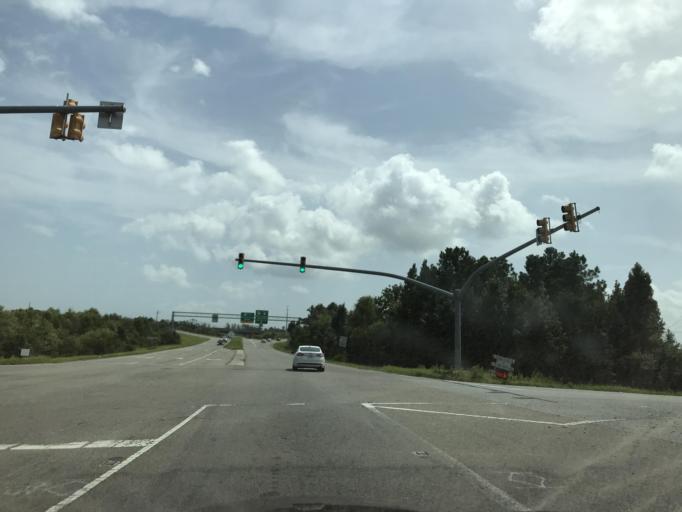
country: US
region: North Carolina
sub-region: New Hanover County
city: Wrightsboro
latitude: 34.2659
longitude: -77.9304
